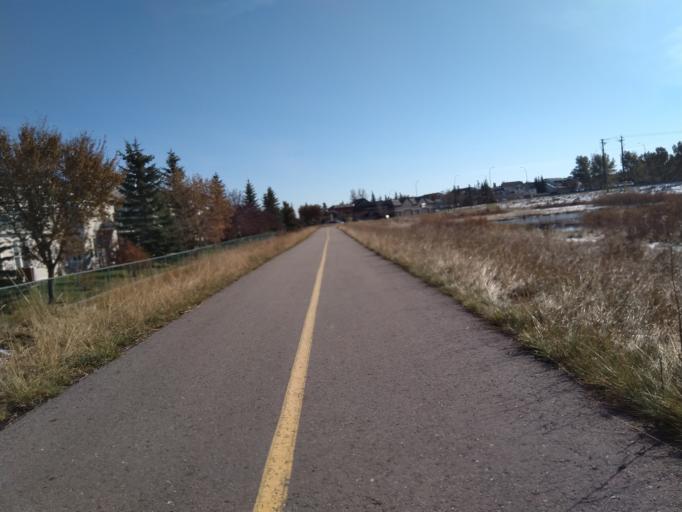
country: CA
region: Alberta
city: Calgary
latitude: 51.1558
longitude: -114.1076
